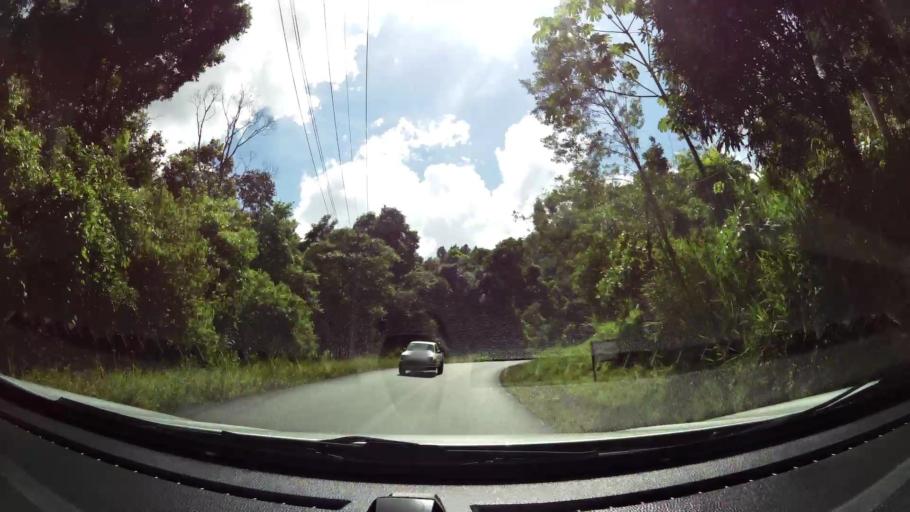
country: CR
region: San Jose
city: San Isidro
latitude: 9.3392
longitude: -83.7373
